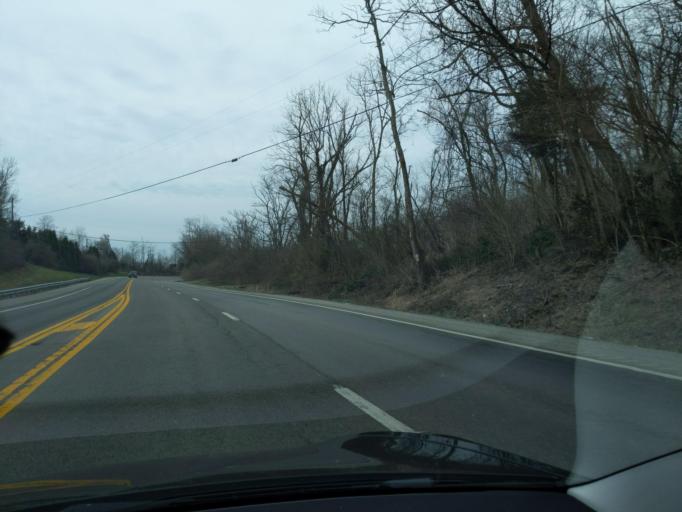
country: US
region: Kentucky
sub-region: Madison County
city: Richmond
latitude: 37.8880
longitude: -84.2854
